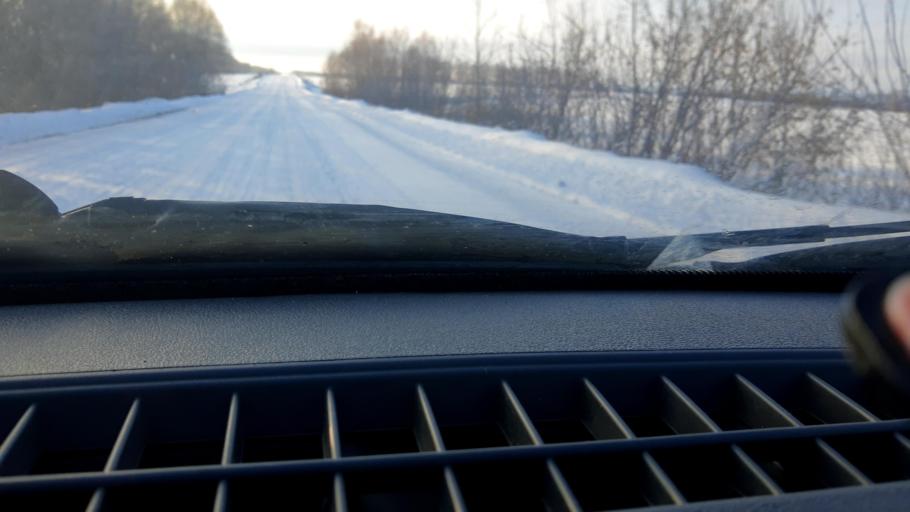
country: RU
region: Bashkortostan
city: Kushnarenkovo
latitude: 55.1215
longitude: 55.5860
